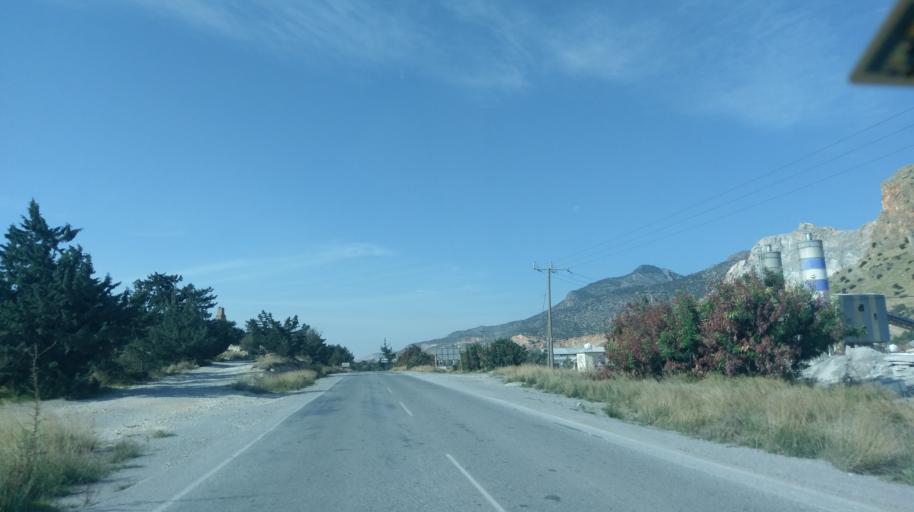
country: CY
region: Lefkosia
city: Nicosia
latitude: 35.2687
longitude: 33.4766
